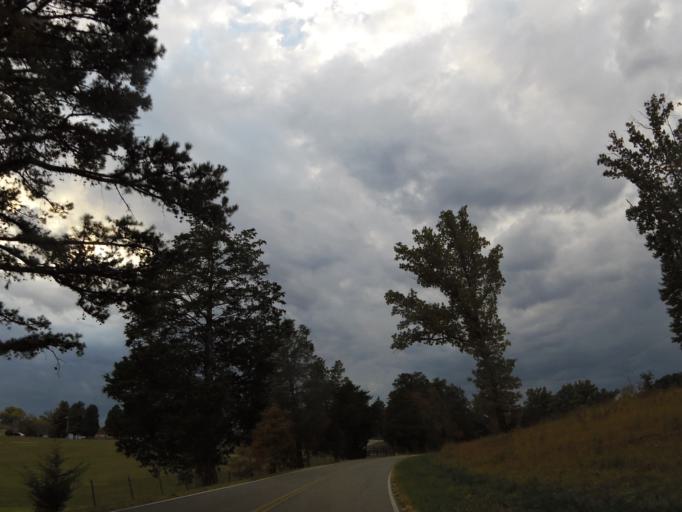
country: US
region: Tennessee
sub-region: Blount County
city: Louisville
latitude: 35.7786
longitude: -84.0814
